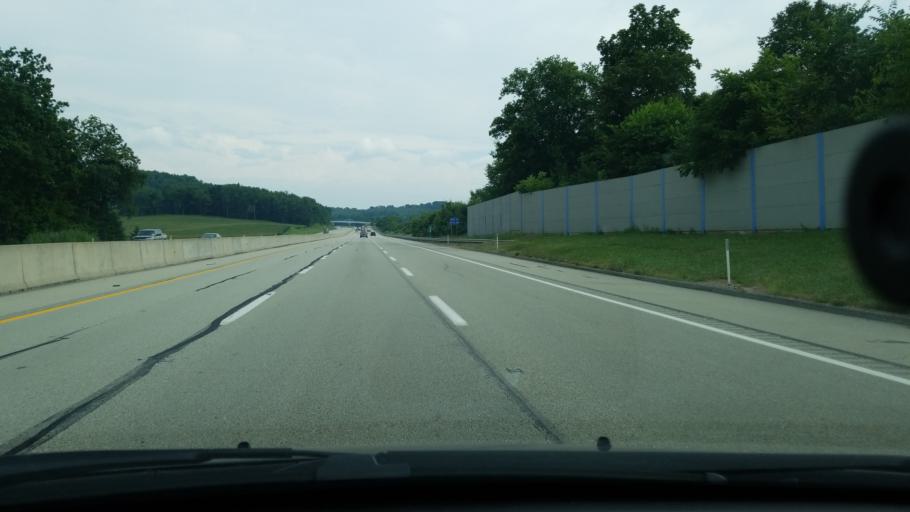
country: US
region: Pennsylvania
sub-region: Lawrence County
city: New Beaver
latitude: 40.8600
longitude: -80.3985
